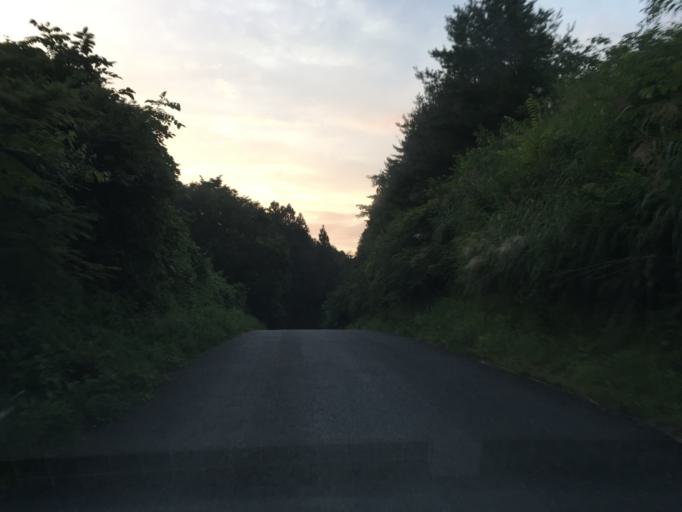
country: JP
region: Iwate
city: Ichinoseki
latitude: 38.8451
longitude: 141.2843
